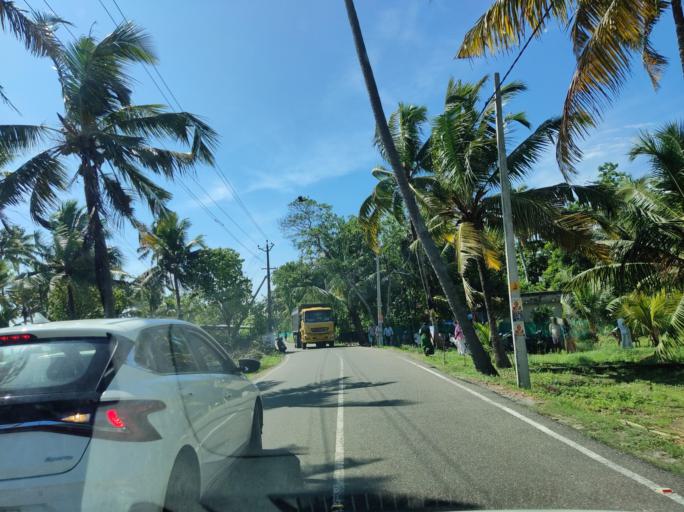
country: IN
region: Kerala
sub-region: Alappuzha
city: Kayankulam
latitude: 9.1956
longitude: 76.4367
